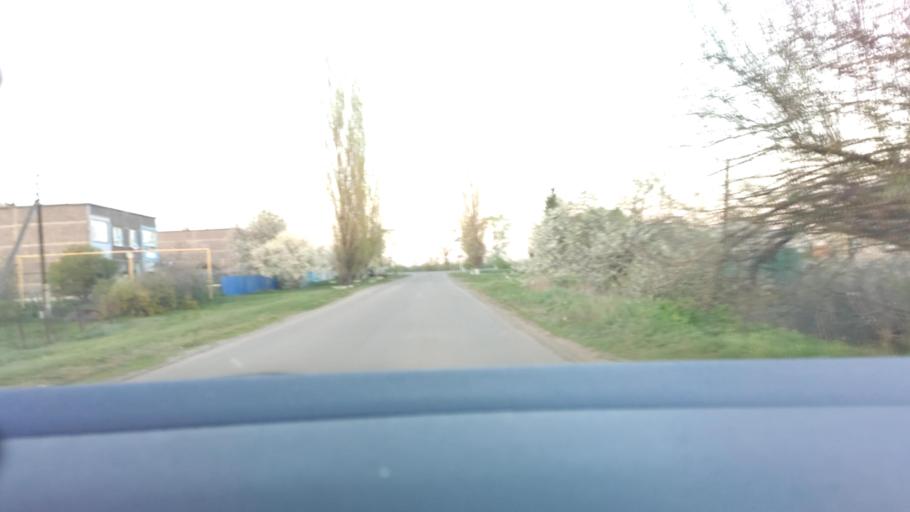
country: RU
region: Voronezj
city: Maslovka
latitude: 51.5041
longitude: 39.3052
